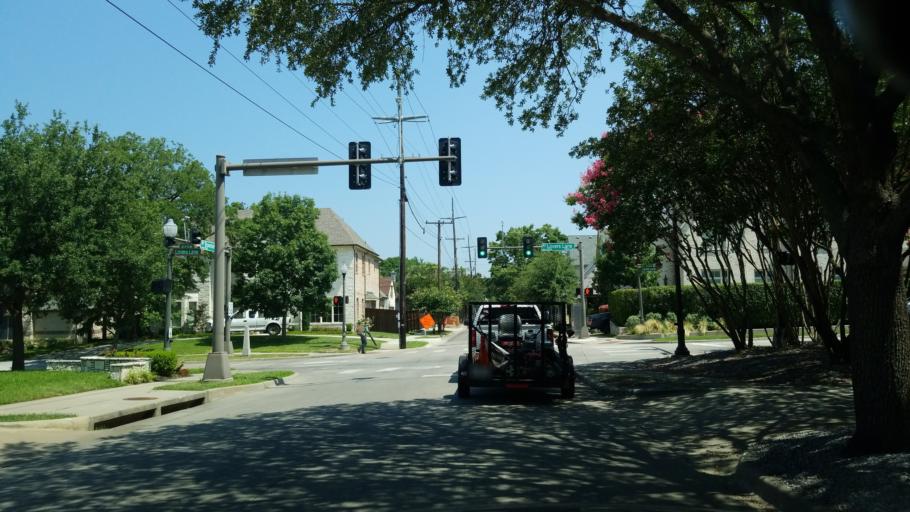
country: US
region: Texas
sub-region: Dallas County
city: Highland Park
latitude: 32.8508
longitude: -96.7770
